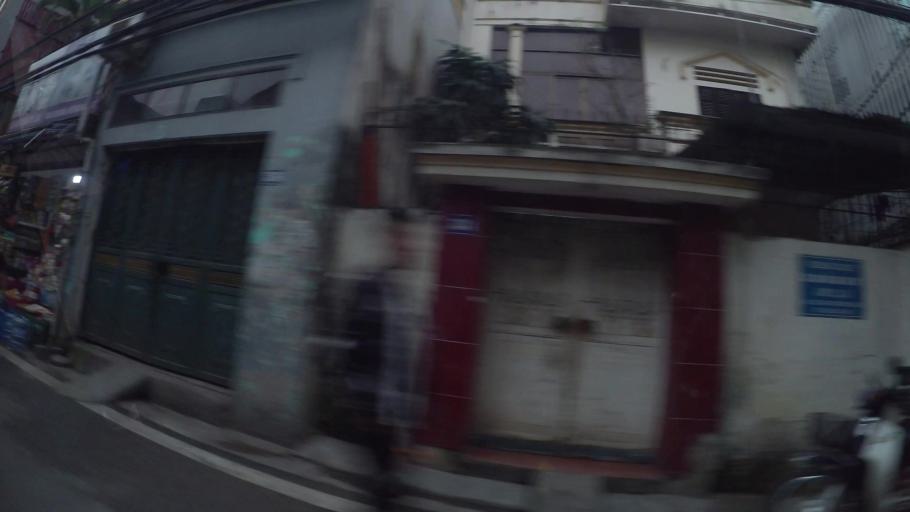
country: VN
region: Ha Noi
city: Hai BaTrung
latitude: 21.0177
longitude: 105.8644
